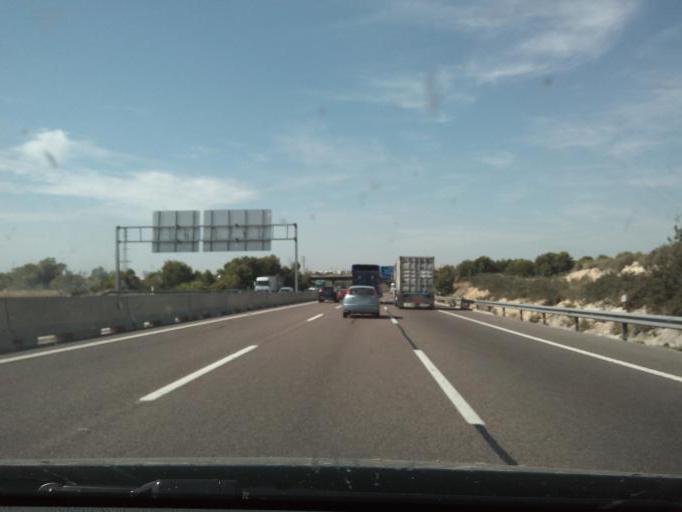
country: ES
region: Valencia
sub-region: Provincia de Valencia
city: Manises
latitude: 39.5280
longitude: -0.4657
